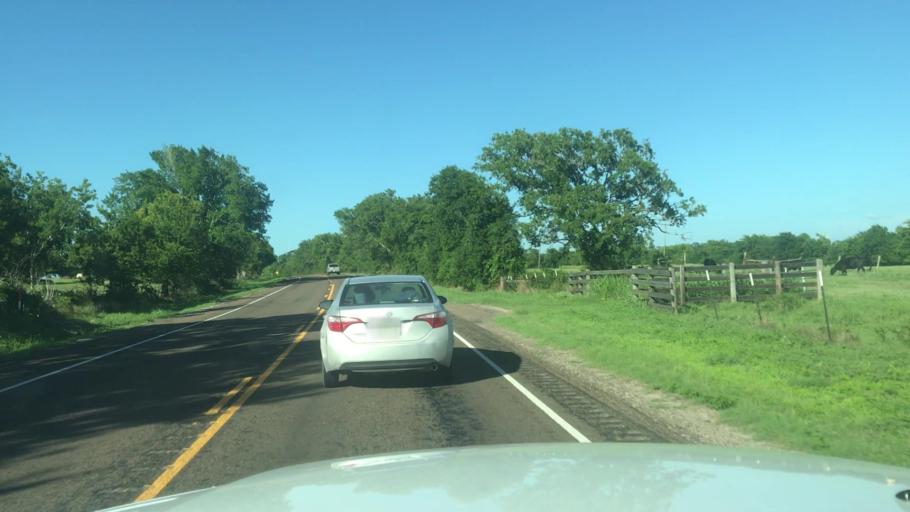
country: US
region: Texas
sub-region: Grimes County
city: Anderson
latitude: 30.6323
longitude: -95.8699
